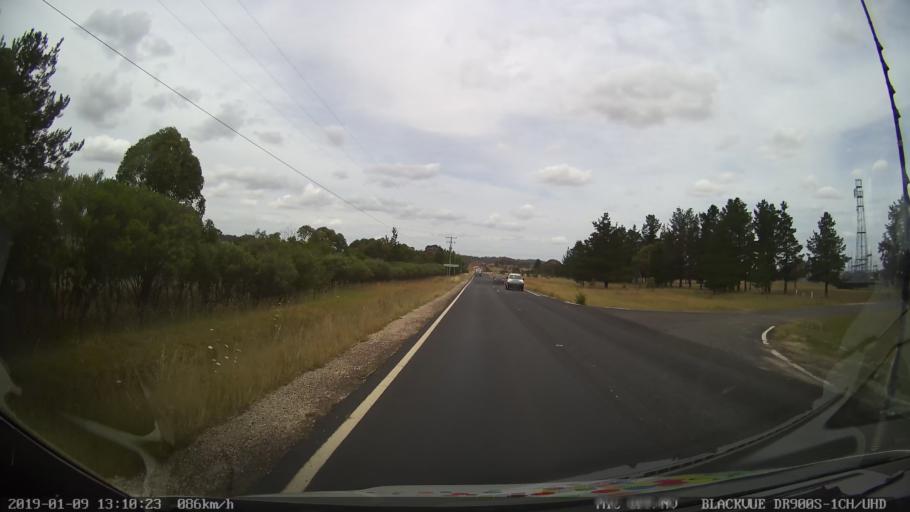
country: AU
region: New South Wales
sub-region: Armidale Dumaresq
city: Armidale
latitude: -30.5294
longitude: 151.7117
